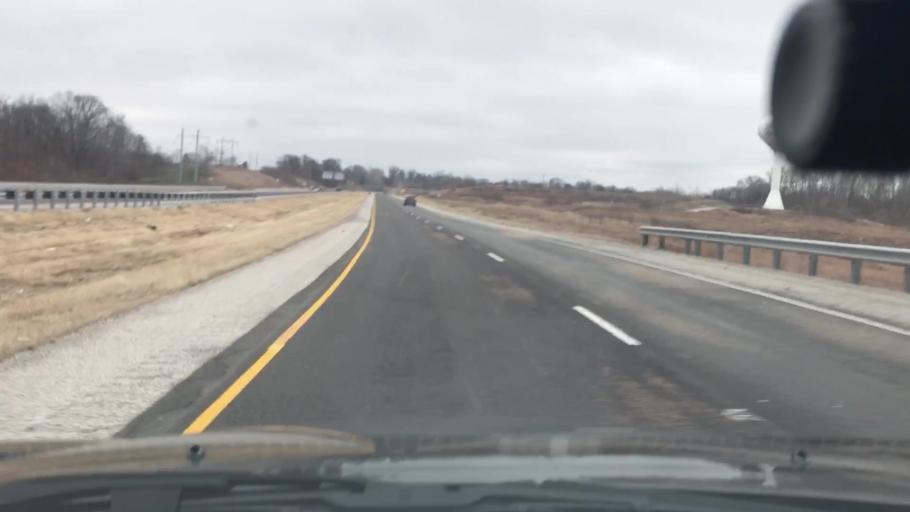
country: US
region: Illinois
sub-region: Madison County
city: Roxana
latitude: 38.8706
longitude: -90.0598
